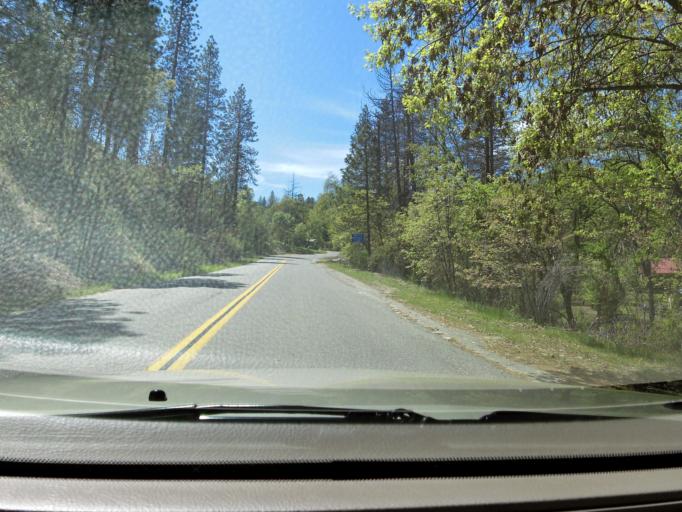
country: US
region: California
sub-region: Fresno County
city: Auberry
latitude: 37.2301
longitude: -119.5124
